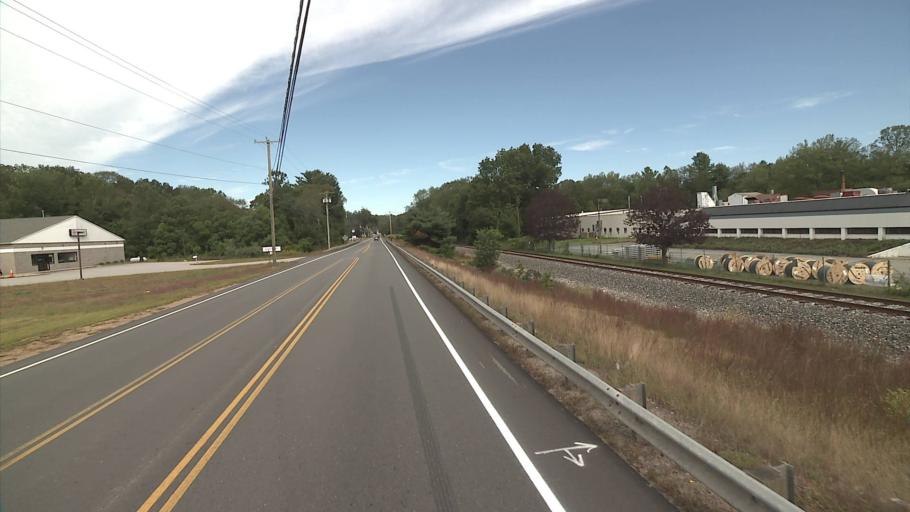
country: US
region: Connecticut
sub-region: Windham County
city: South Windham
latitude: 41.6865
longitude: -72.1742
